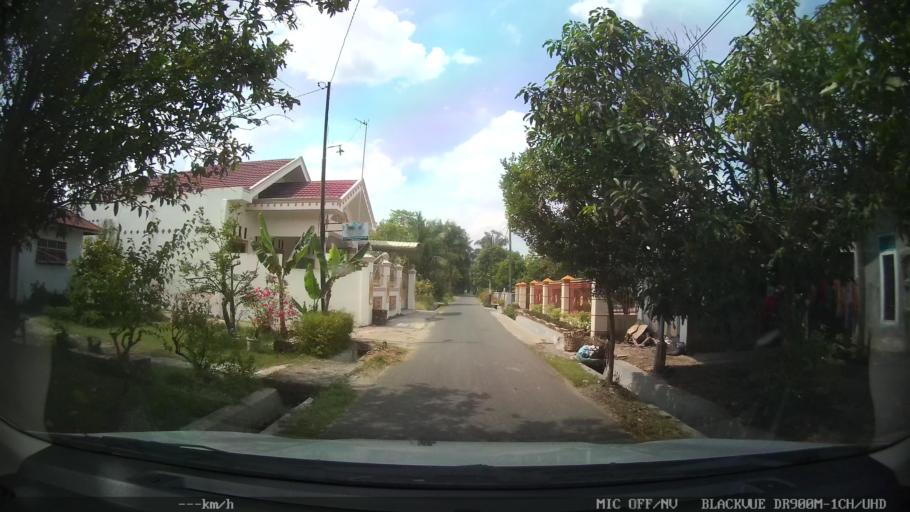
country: ID
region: North Sumatra
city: Binjai
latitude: 3.6218
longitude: 98.5165
